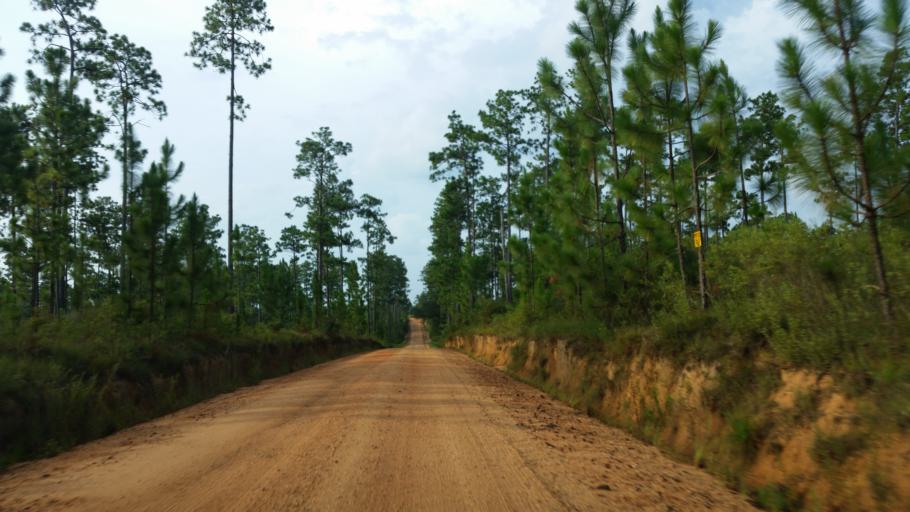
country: US
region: Alabama
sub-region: Escambia County
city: Atmore
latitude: 30.8686
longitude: -87.5817
